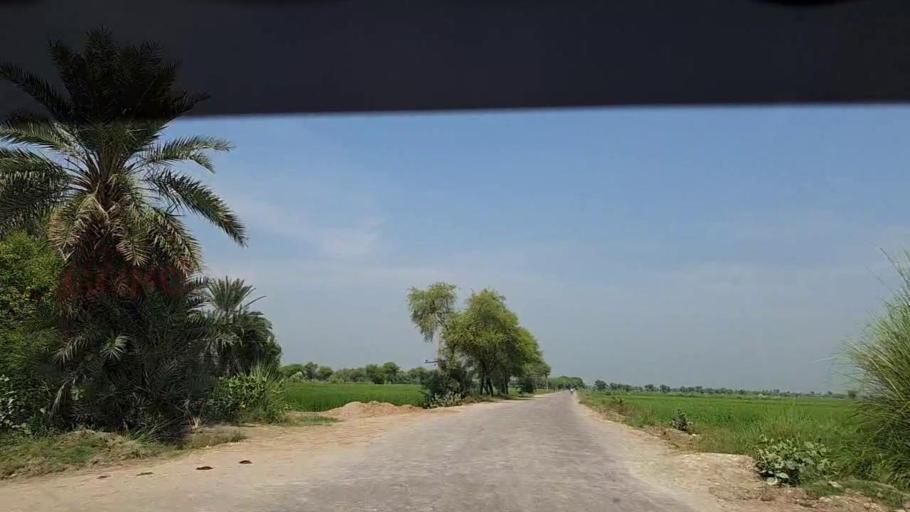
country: PK
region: Sindh
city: Thul
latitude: 28.1363
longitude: 68.7167
